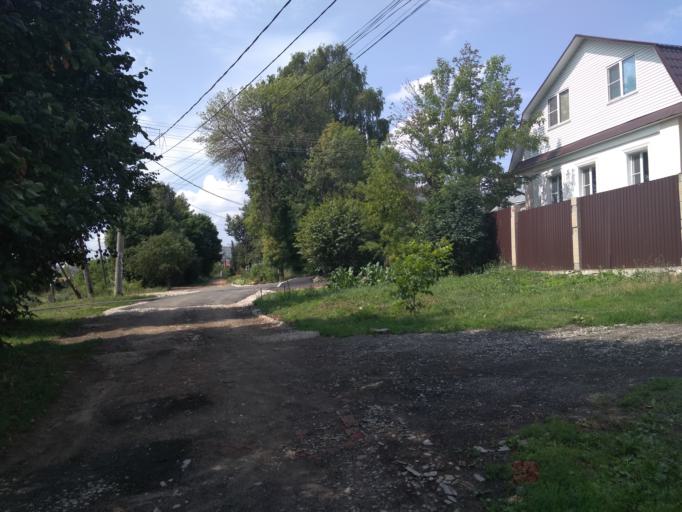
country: RU
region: Tula
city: Mendeleyevskiy
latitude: 54.1623
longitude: 37.6108
